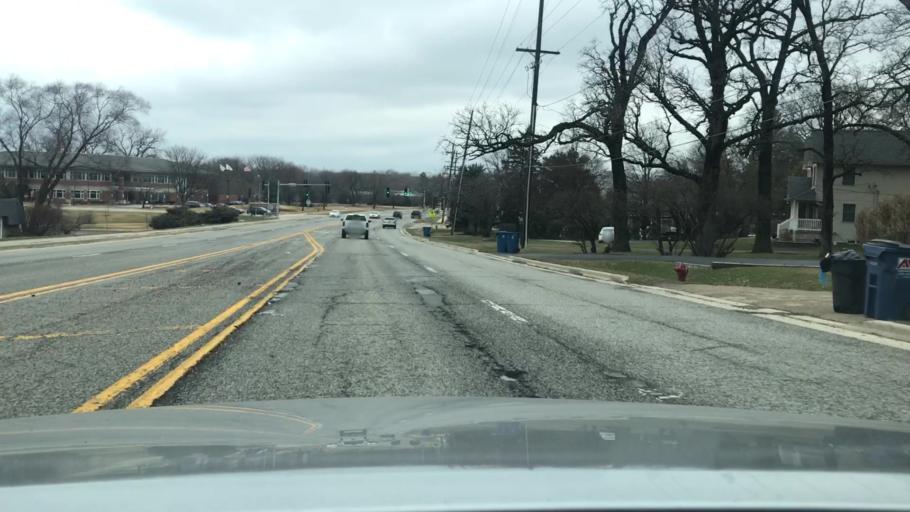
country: US
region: Illinois
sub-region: DuPage County
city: Lisle
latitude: 41.7923
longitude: -88.0755
